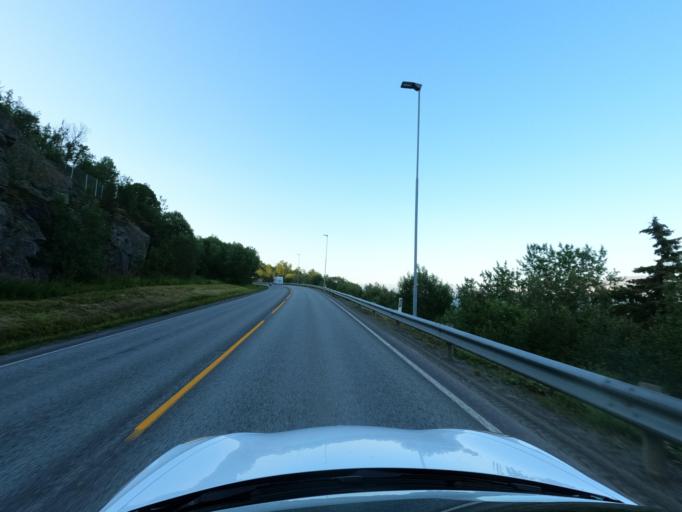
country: NO
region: Troms
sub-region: Harstad
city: Harstad
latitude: 68.7508
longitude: 16.5657
